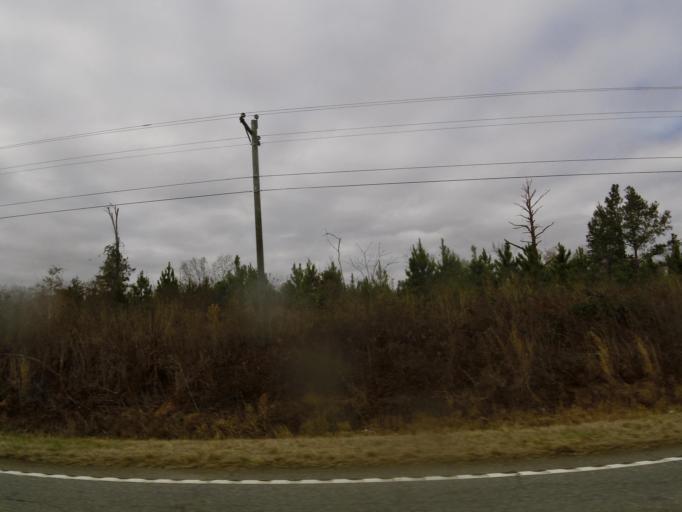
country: US
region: Georgia
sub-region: Quitman County
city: Georgetown
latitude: 31.8574
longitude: -85.0437
